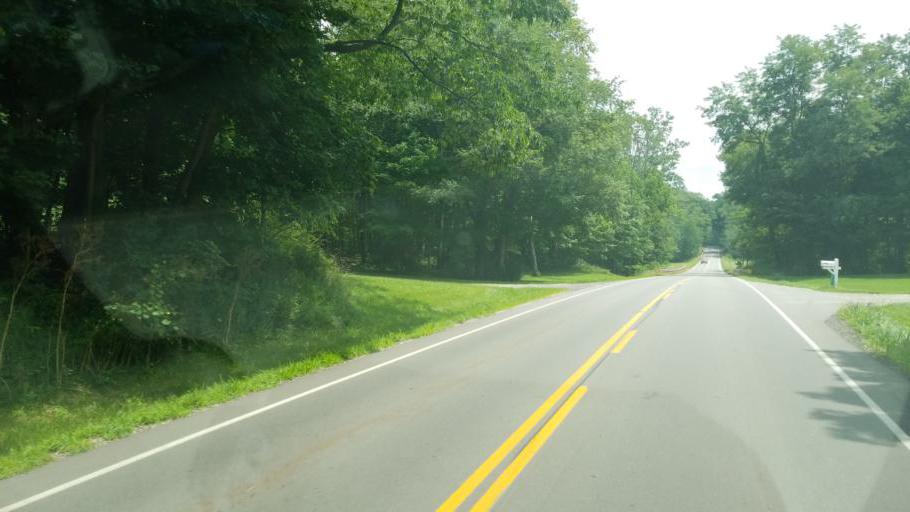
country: US
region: Ohio
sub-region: Richland County
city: Lexington
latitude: 40.7018
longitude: -82.6326
